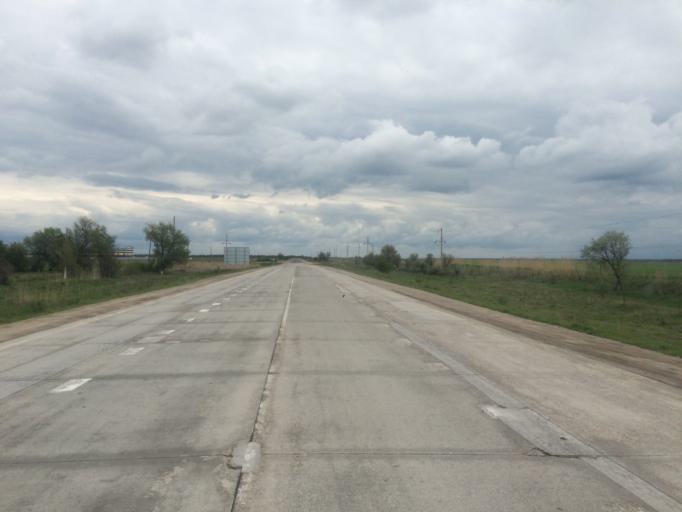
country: KG
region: Chuy
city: Sokuluk
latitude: 43.2708
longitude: 74.2413
